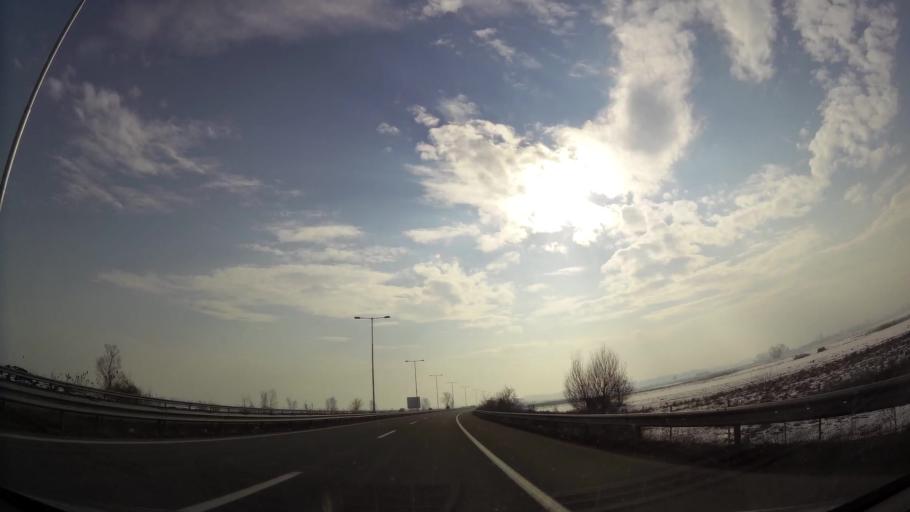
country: MK
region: Aracinovo
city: Arachinovo
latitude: 42.0068
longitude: 21.5350
